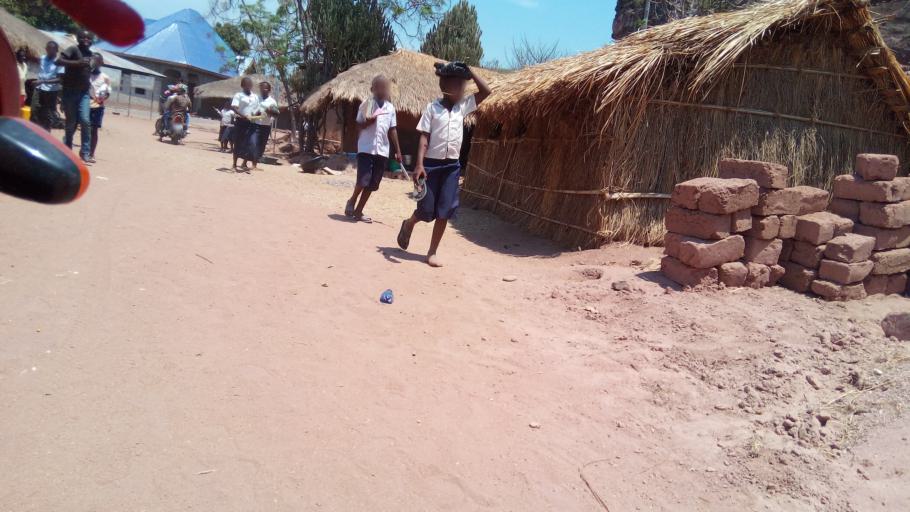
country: CD
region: Katanga
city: Kalemie
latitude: -5.9905
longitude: 29.1939
